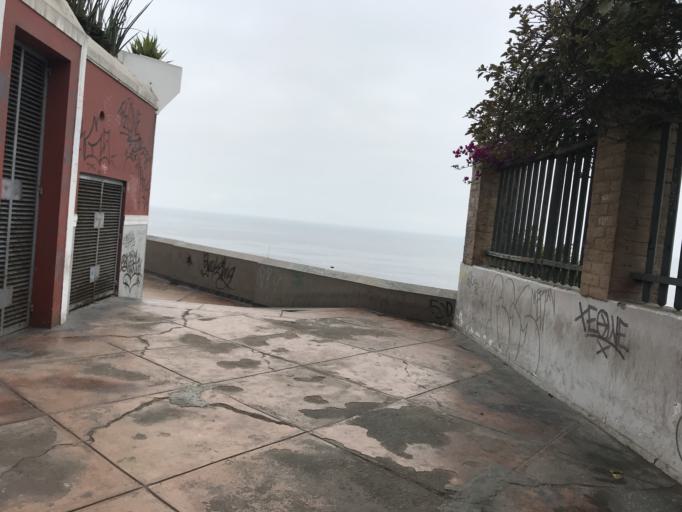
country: PE
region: Lima
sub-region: Lima
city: Surco
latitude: -12.1518
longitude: -77.0238
